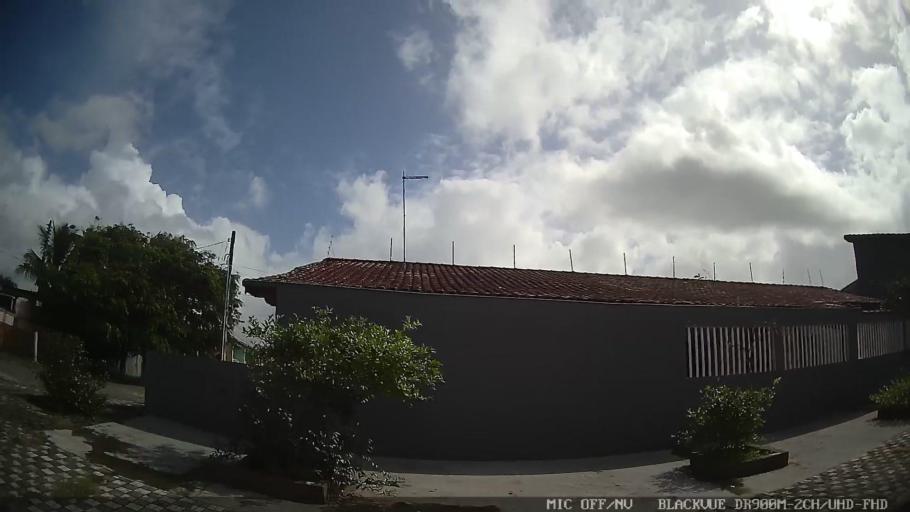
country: BR
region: Sao Paulo
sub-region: Mongagua
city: Mongagua
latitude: -24.1317
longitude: -46.6914
